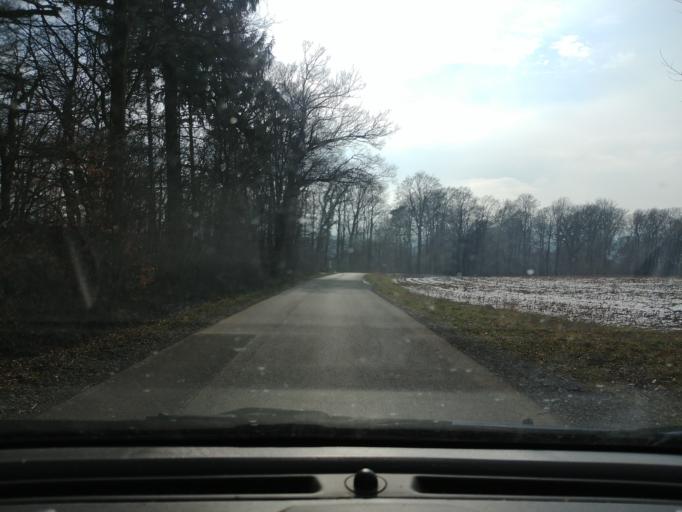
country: DE
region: Lower Saxony
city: Bad Karlshafen
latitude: 51.6534
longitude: 9.4383
